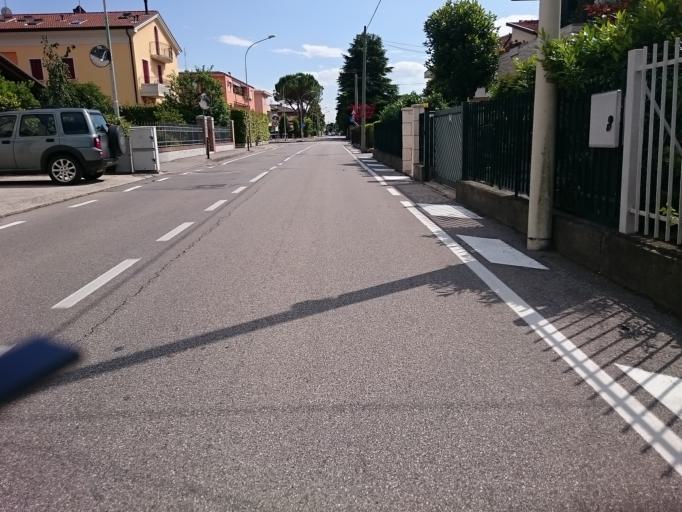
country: IT
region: Veneto
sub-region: Provincia di Padova
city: Caselle
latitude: 45.4168
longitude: 11.8094
